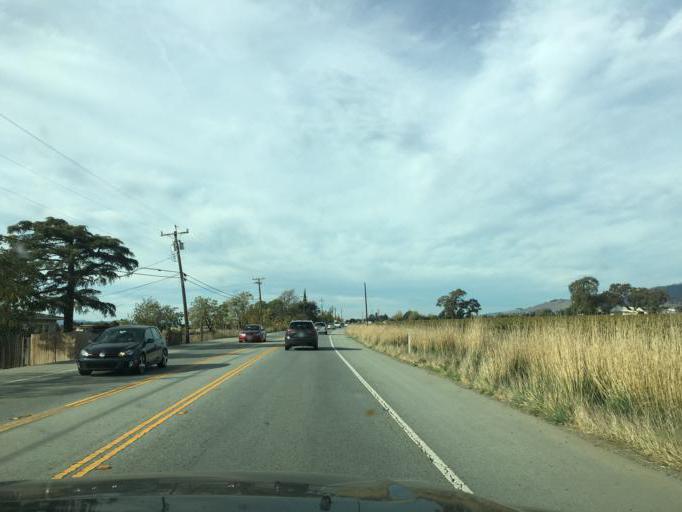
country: US
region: California
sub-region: Santa Clara County
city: Gilroy
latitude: 36.9953
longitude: -121.4999
